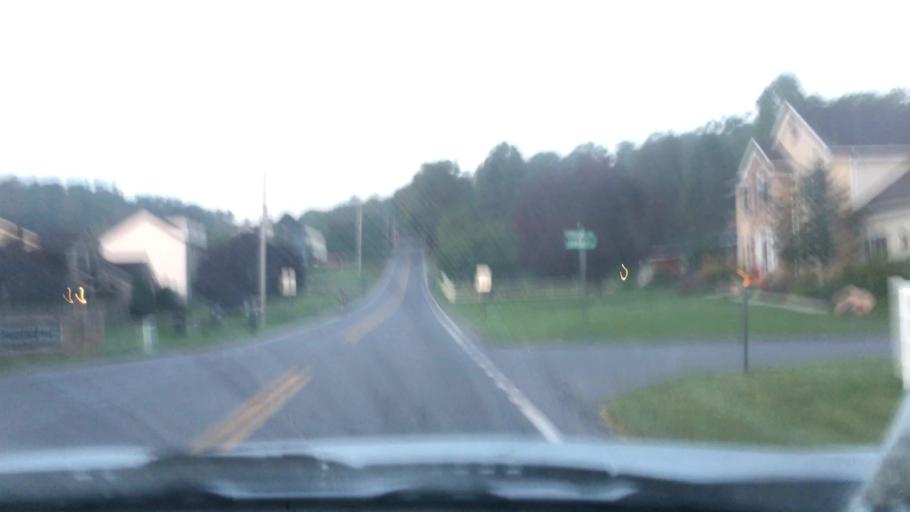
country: US
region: Pennsylvania
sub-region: Blair County
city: Duncansville
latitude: 40.4148
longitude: -78.4205
